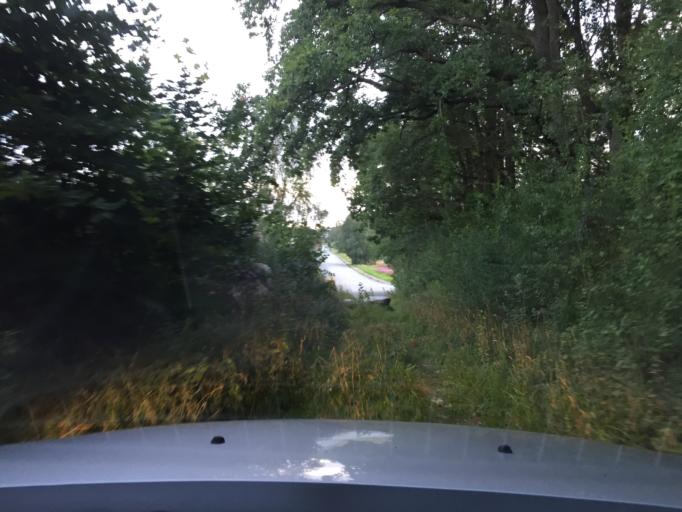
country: SE
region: Skane
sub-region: Hassleholms Kommun
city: Sosdala
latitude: 56.0384
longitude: 13.6903
